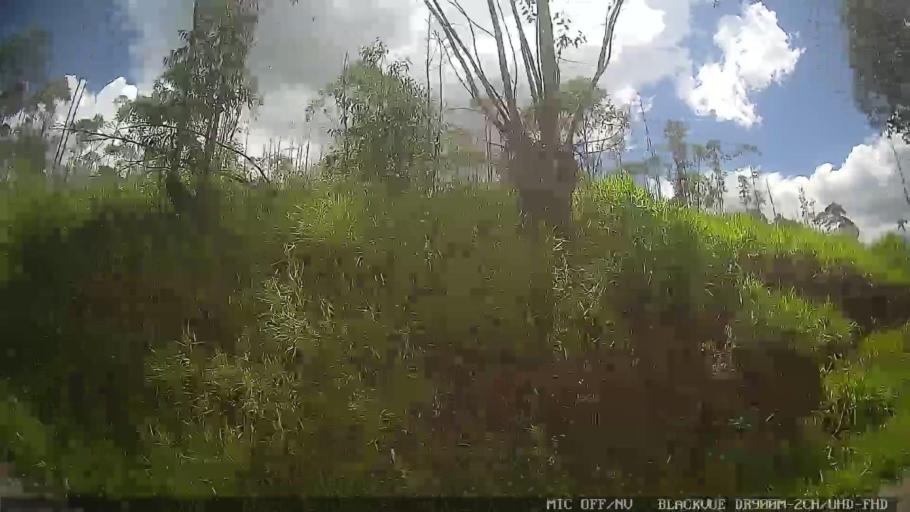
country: BR
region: Sao Paulo
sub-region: Braganca Paulista
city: Braganca Paulista
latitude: -22.9937
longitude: -46.4562
